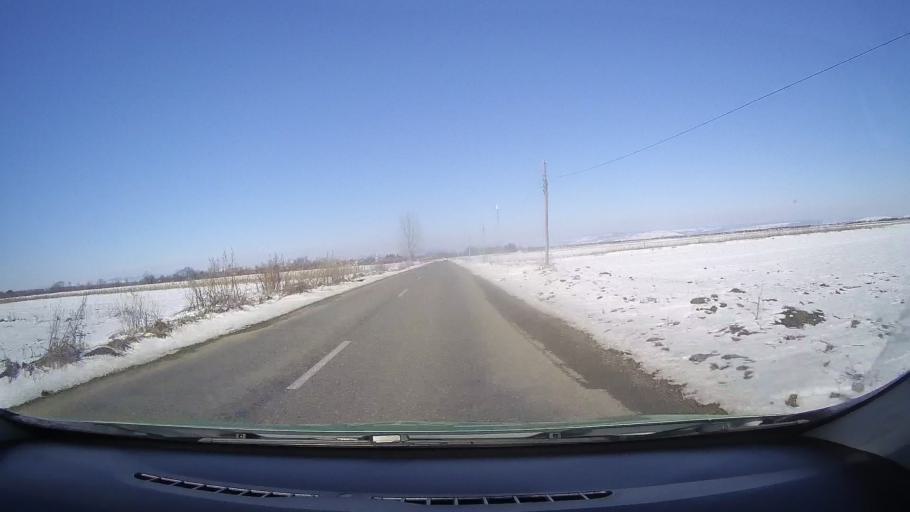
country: RO
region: Brasov
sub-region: Comuna Harseni
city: Harseni
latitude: 45.7453
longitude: 25.0177
